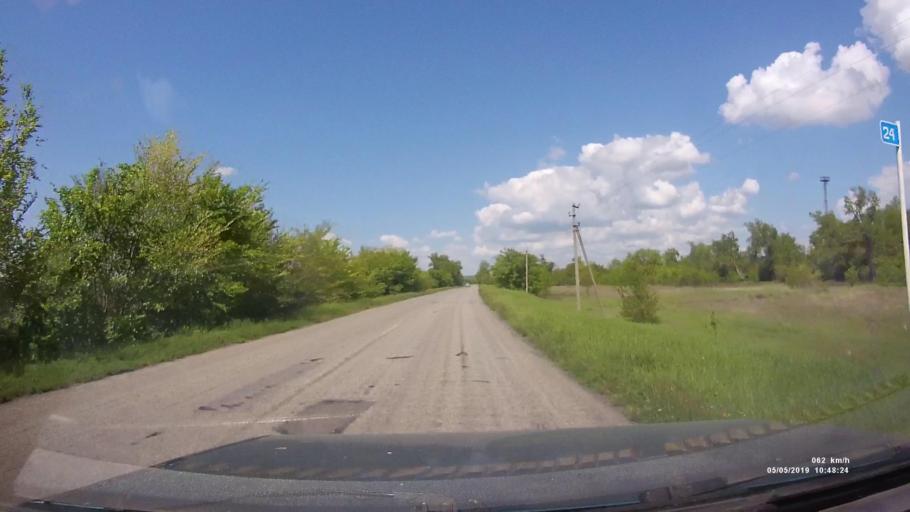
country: RU
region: Rostov
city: Ust'-Donetskiy
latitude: 47.6425
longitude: 40.8204
